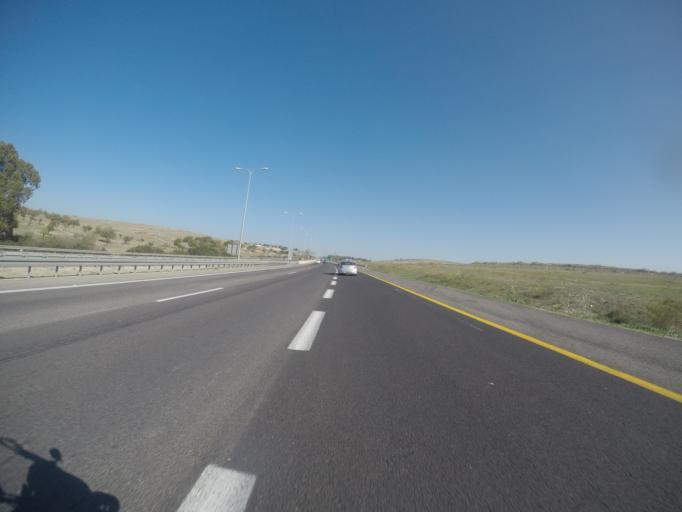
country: IL
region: Haifa
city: Daliyat el Karmil
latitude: 32.6195
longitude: 35.0557
